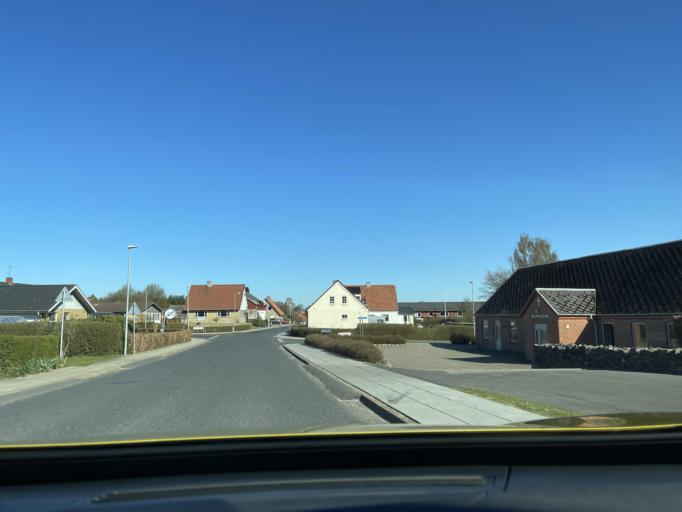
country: DK
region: Central Jutland
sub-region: Silkeborg Kommune
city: Kjellerup
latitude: 56.2535
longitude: 9.4276
